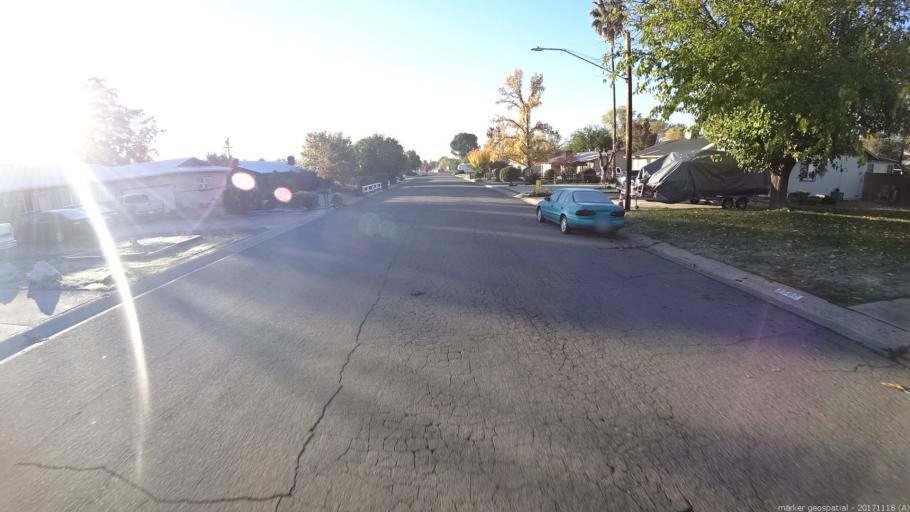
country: US
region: California
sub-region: Shasta County
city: Cottonwood
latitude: 40.3910
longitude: -122.2903
